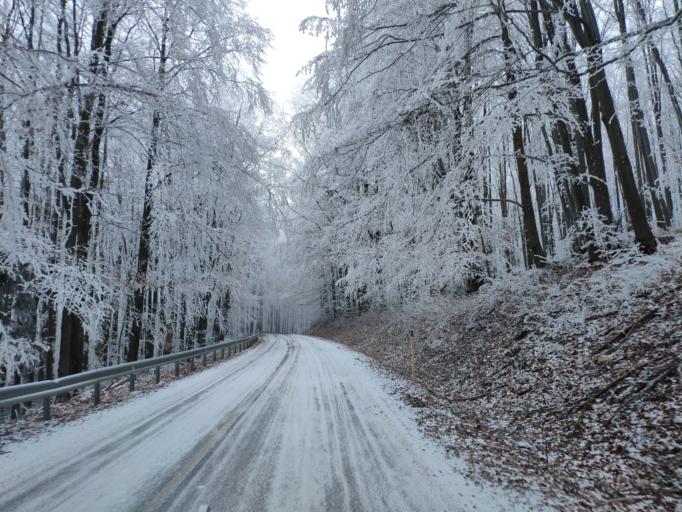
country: SK
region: Kosicky
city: Dobsina
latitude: 48.8076
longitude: 20.4832
